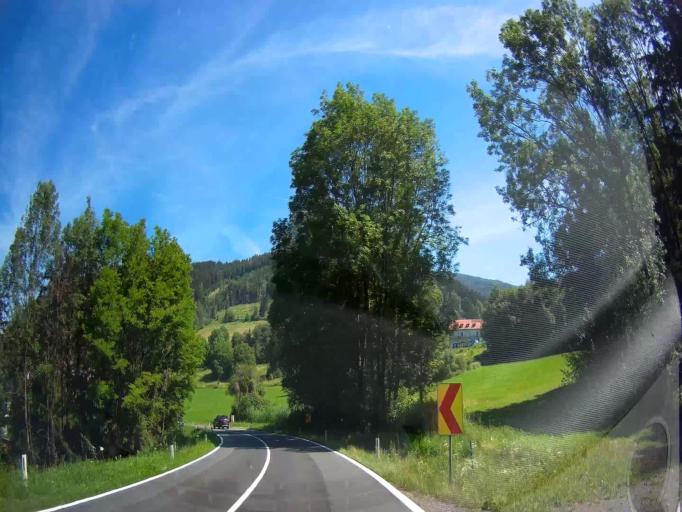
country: AT
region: Carinthia
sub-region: Politischer Bezirk Sankt Veit an der Glan
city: Althofen
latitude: 46.8936
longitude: 14.4452
